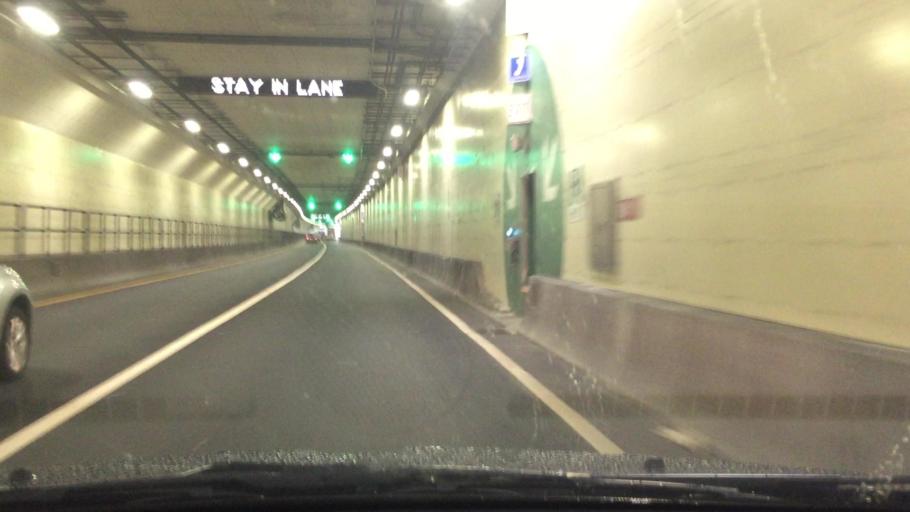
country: US
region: Virginia
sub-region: City of Portsmouth
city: Portsmouth
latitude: 36.8592
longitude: -76.3140
